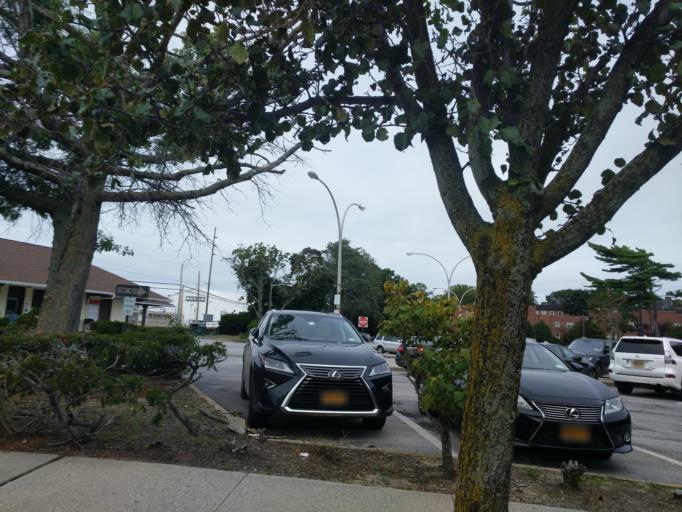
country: US
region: New York
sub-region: Nassau County
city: Lawrence
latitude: 40.6146
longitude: -73.7368
